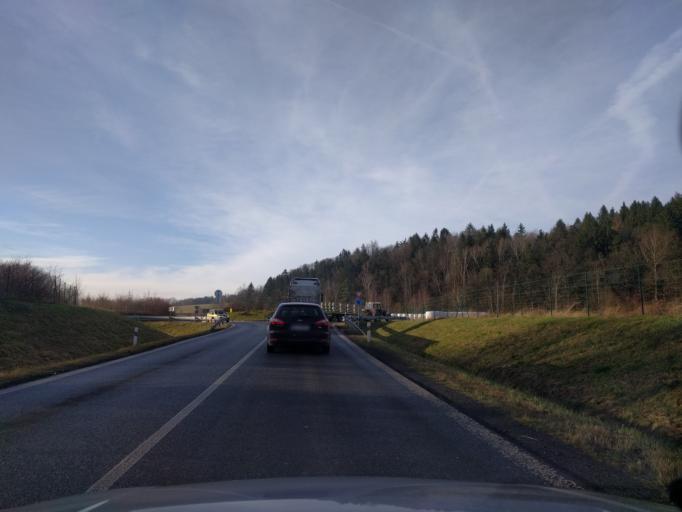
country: CZ
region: Liberecky
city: Mnisek
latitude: 50.8189
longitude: 15.0369
